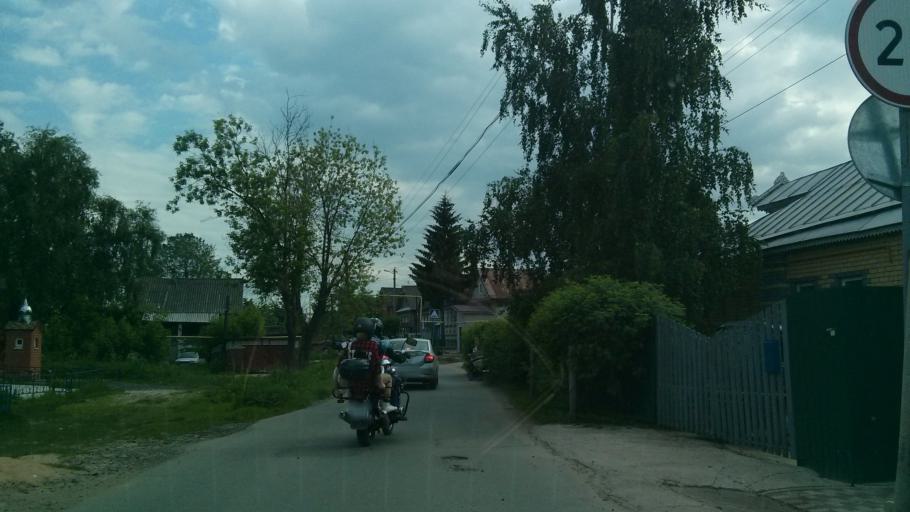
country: RU
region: Nizjnij Novgorod
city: Afonino
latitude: 56.2882
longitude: 44.0997
